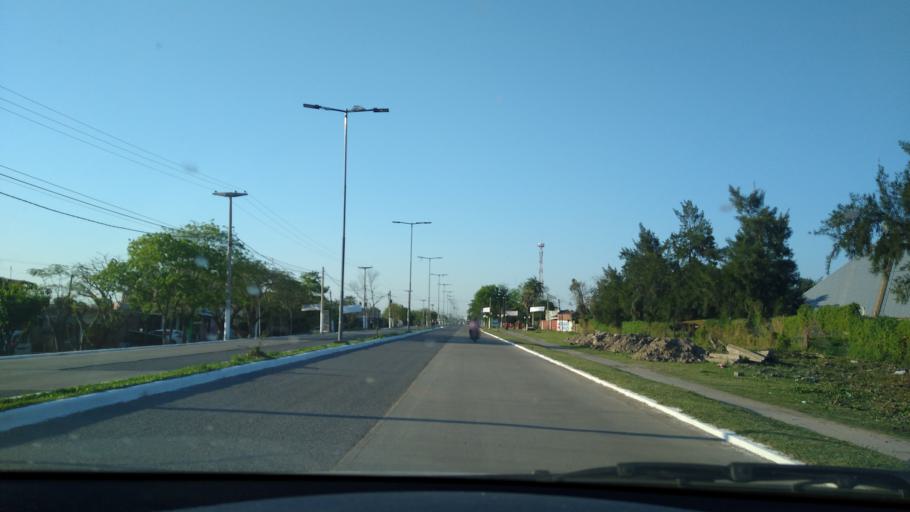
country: AR
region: Chaco
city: Puerto Vilelas
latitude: -27.5148
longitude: -58.9418
